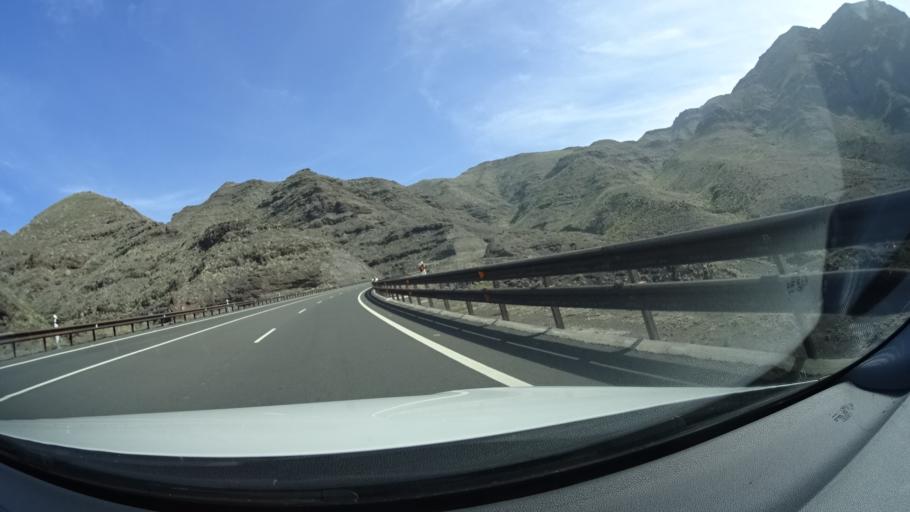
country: ES
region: Canary Islands
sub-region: Provincia de Las Palmas
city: San Nicolas
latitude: 28.0184
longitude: -15.7704
